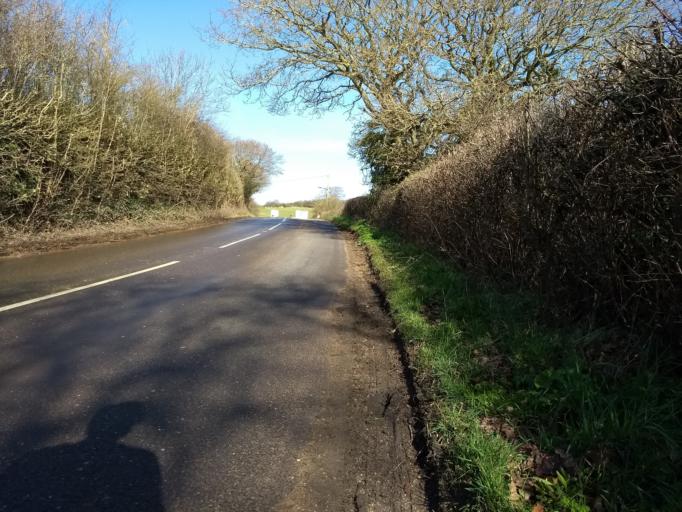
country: GB
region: England
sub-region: Isle of Wight
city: Seaview
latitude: 50.7023
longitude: -1.1077
